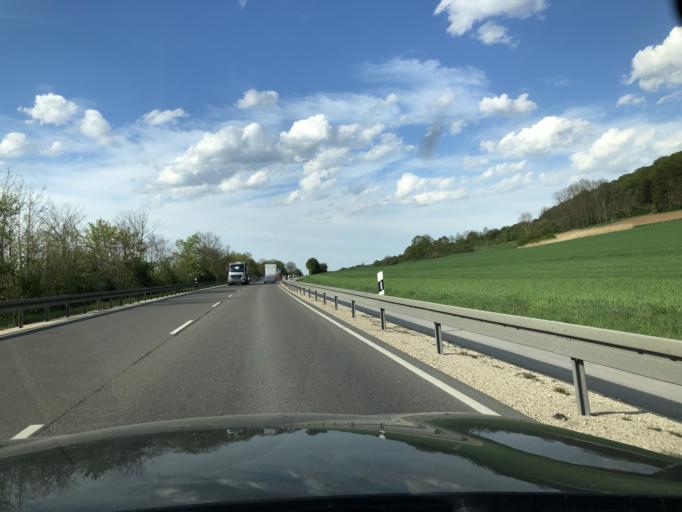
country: DE
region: Bavaria
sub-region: Regierungsbezirk Mittelfranken
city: Weissenburg in Bayern
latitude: 49.0038
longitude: 10.9536
